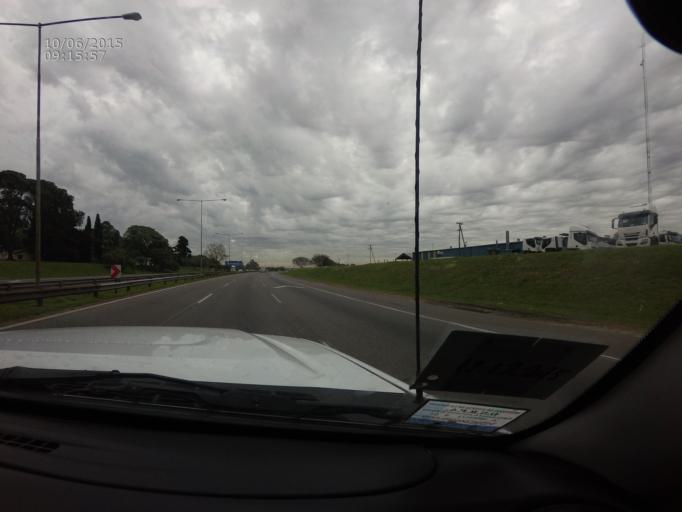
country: AR
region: Buenos Aires
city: Belen de Escobar
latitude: -34.3186
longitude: -58.8658
